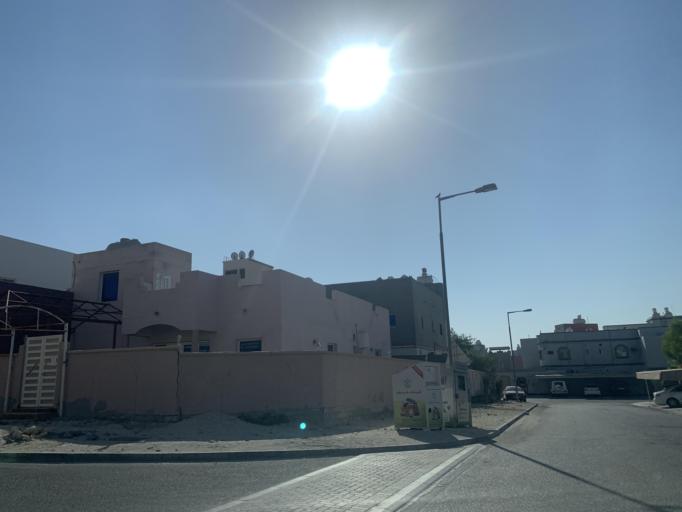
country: BH
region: Central Governorate
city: Madinat Hamad
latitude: 26.1044
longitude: 50.5099
